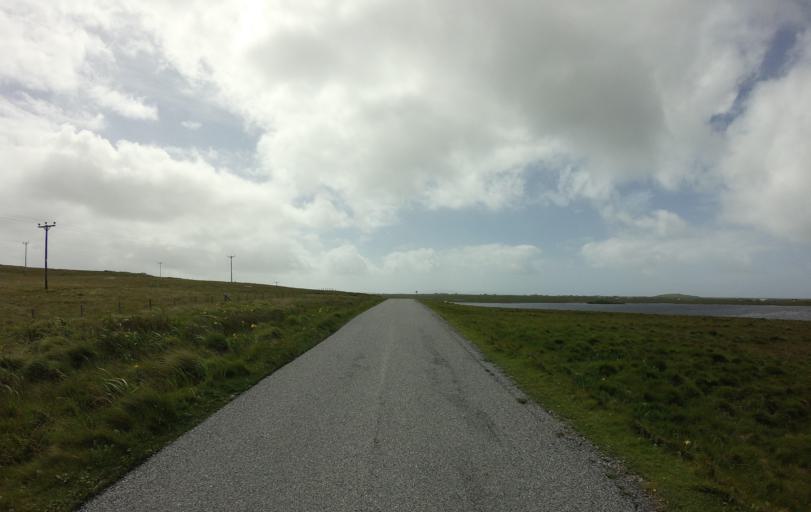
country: GB
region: Scotland
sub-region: Eilean Siar
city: Isle of South Uist
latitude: 57.1454
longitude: -7.3725
